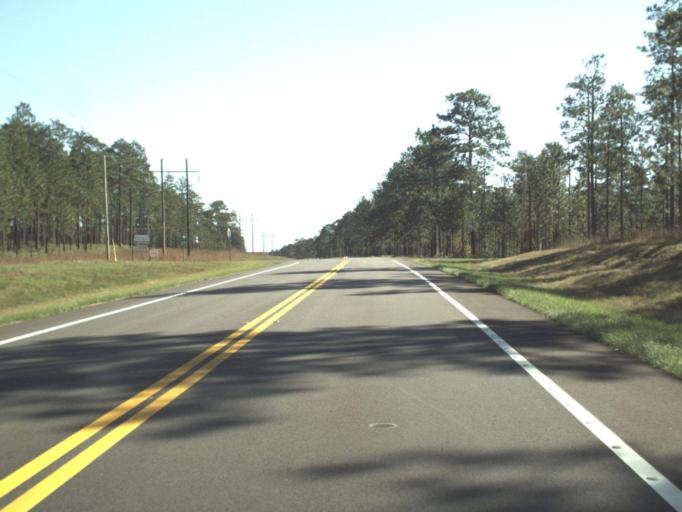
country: US
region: Florida
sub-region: Santa Rosa County
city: Point Baker
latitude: 30.8735
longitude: -86.9384
